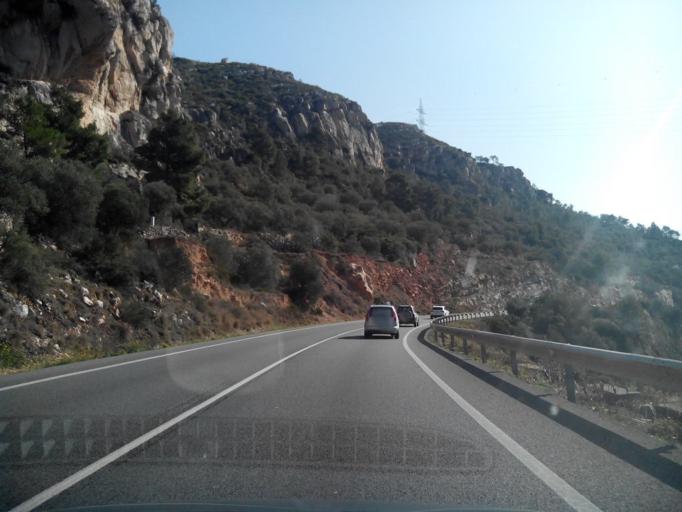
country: ES
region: Catalonia
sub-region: Provincia de Tarragona
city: Alcover
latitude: 41.3130
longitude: 1.1873
